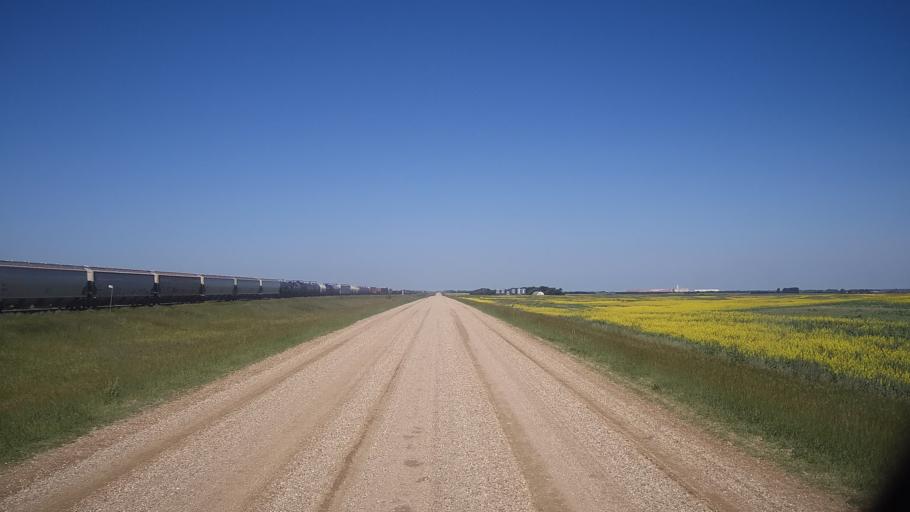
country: CA
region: Saskatchewan
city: Watrous
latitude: 51.8587
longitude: -105.9582
